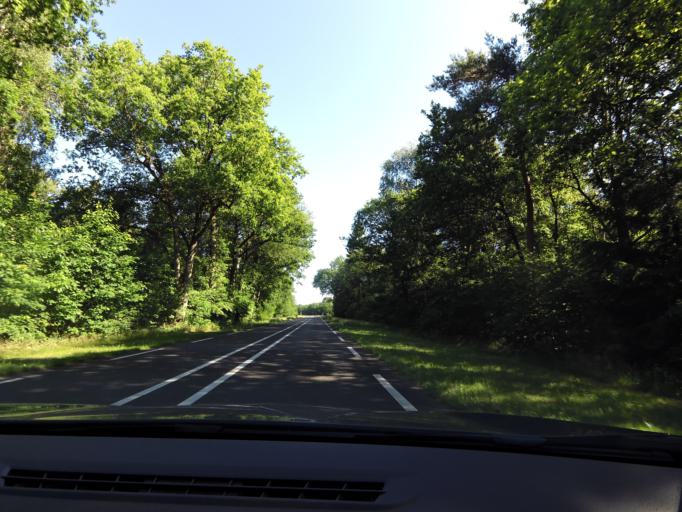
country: NL
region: Overijssel
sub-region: Gemeente Twenterand
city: Den Ham
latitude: 52.4841
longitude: 6.4273
